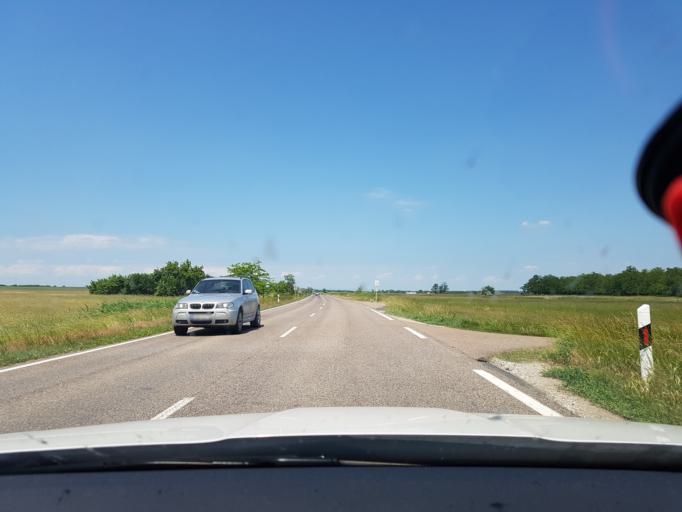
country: HU
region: Hajdu-Bihar
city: Egyek
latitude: 47.5696
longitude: 20.8605
